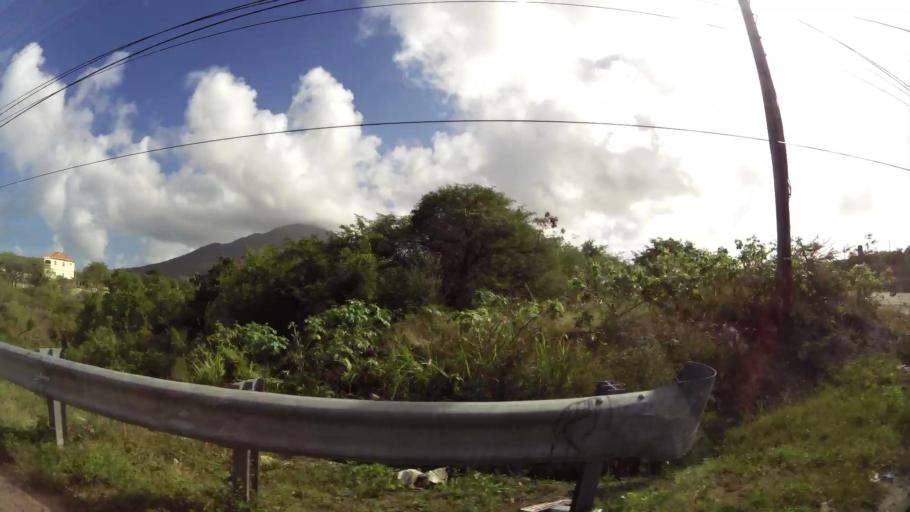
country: KN
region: Saint Paul Charlestown
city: Charlestown
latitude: 17.1254
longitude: -62.6188
